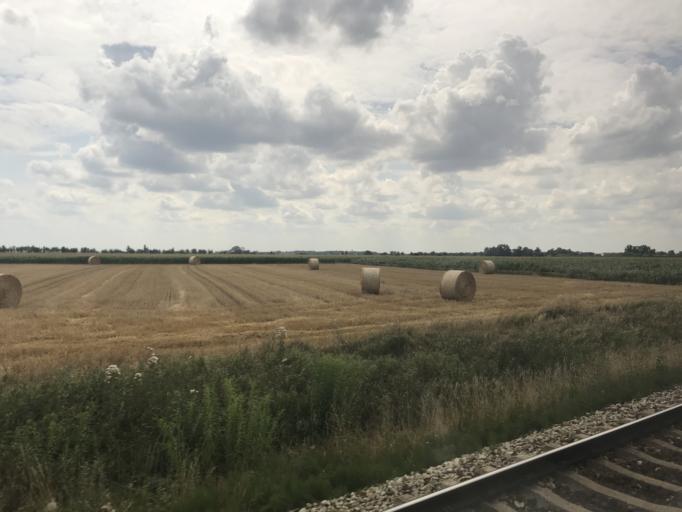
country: PL
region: Greater Poland Voivodeship
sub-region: Powiat poznanski
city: Dopiewo
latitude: 52.3700
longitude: 16.7239
